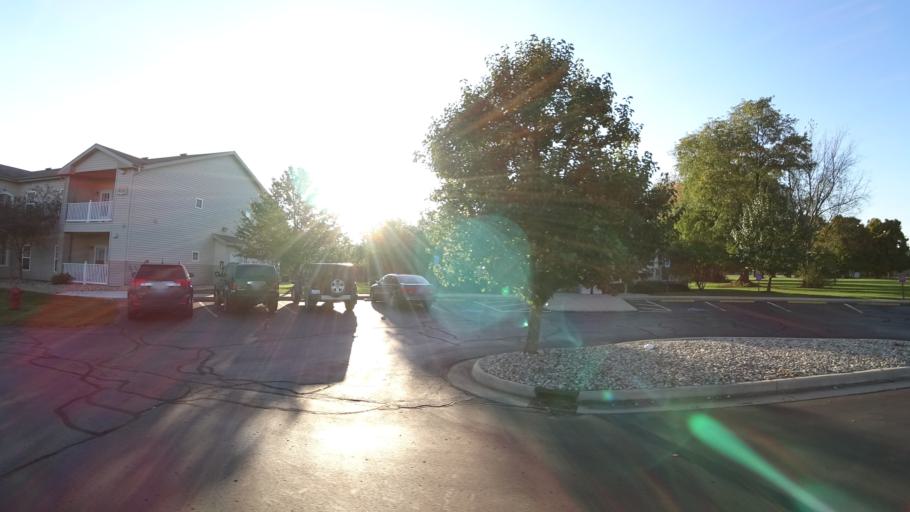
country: US
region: Michigan
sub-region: Saint Joseph County
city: Three Rivers
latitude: 41.9468
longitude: -85.6474
